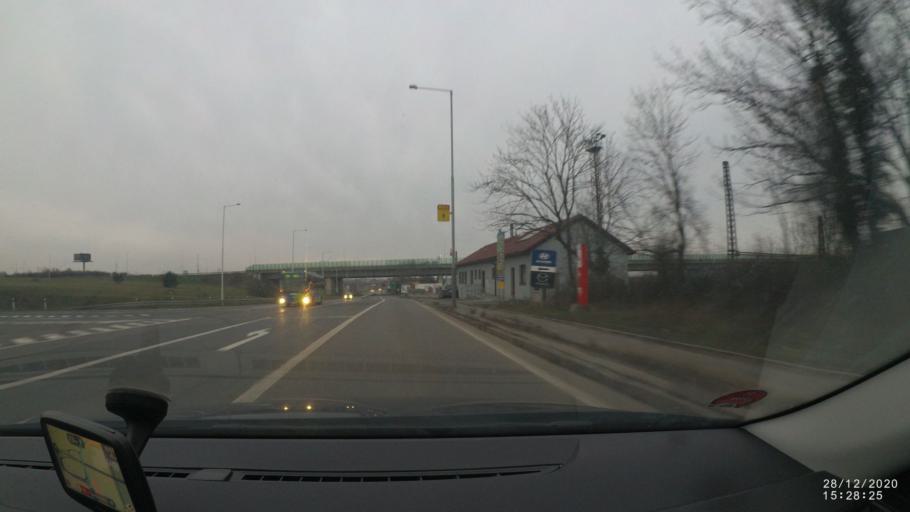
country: CZ
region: Praha
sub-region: Praha 14
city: Dolni Pocernice
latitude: 50.0813
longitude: 14.5962
